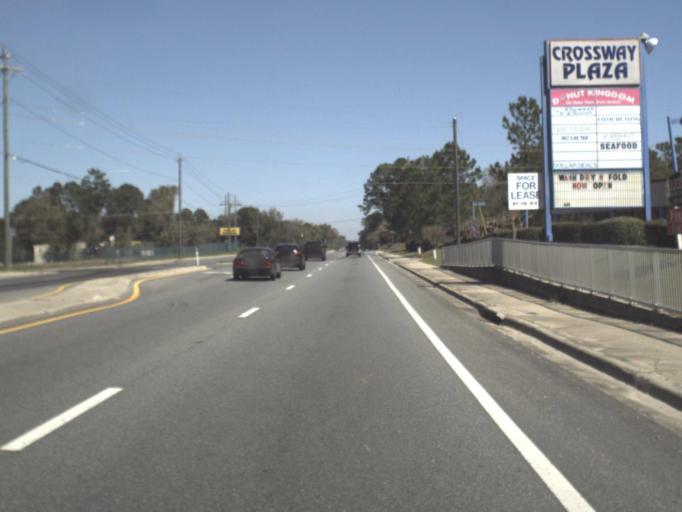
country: US
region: Florida
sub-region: Leon County
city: Tallahassee
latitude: 30.3789
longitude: -84.2910
